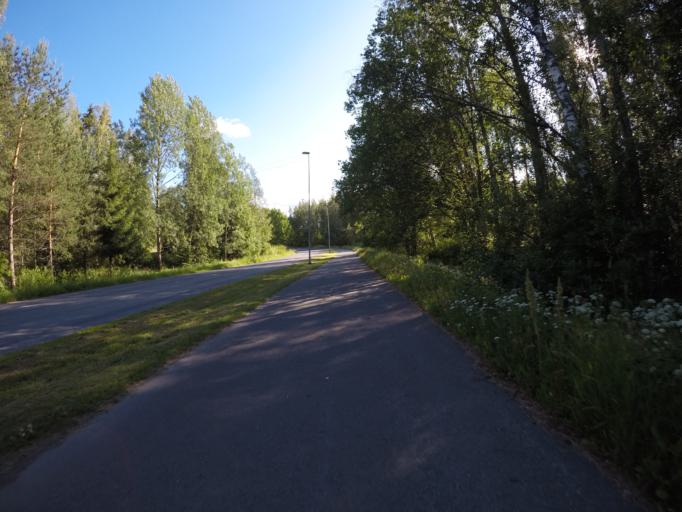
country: FI
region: Haeme
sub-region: Haemeenlinna
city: Haemeenlinna
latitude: 61.0167
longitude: 24.4991
